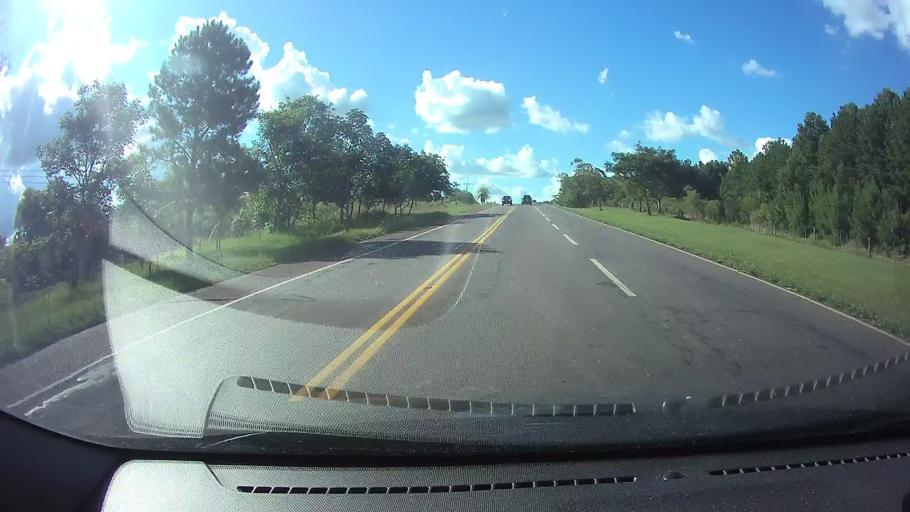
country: PY
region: Cordillera
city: Itacurubi de la Cordillera
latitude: -25.4506
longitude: -56.9007
